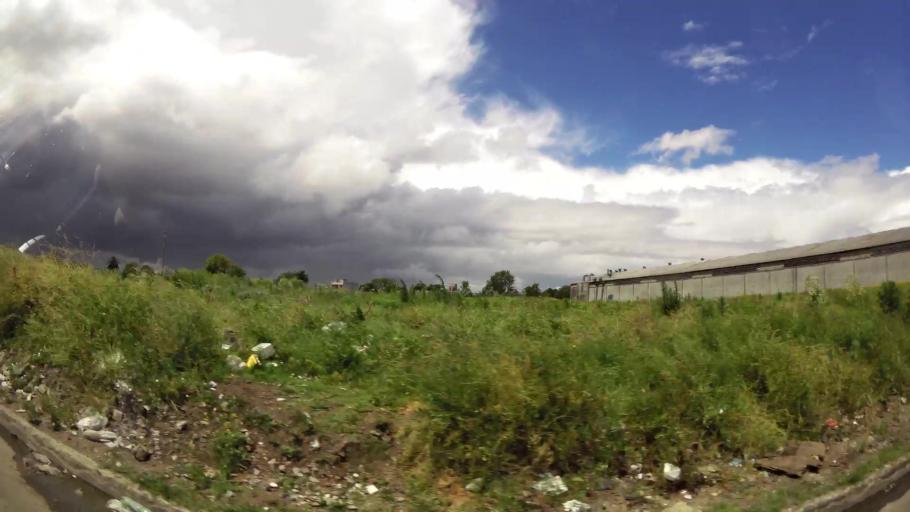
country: UY
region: Montevideo
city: Montevideo
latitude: -34.8396
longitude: -56.1708
